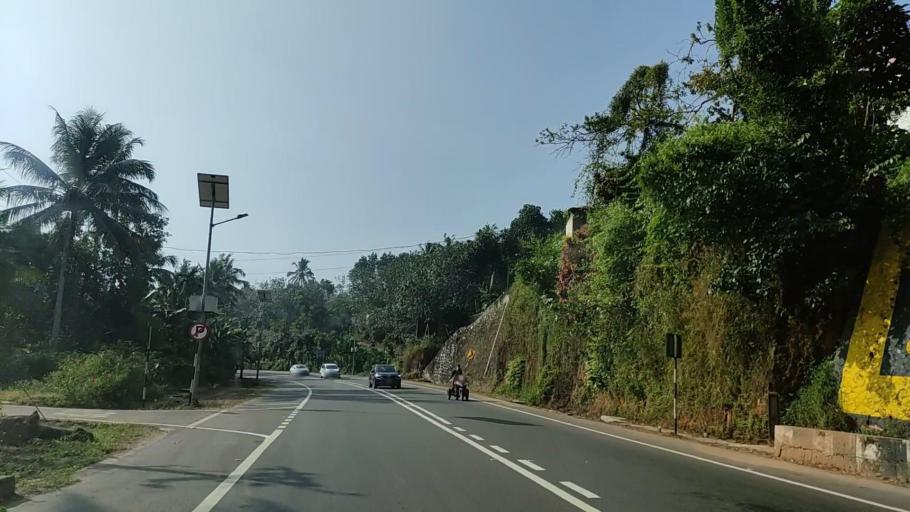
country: IN
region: Kerala
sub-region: Kollam
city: Punalur
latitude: 8.9712
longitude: 76.8286
